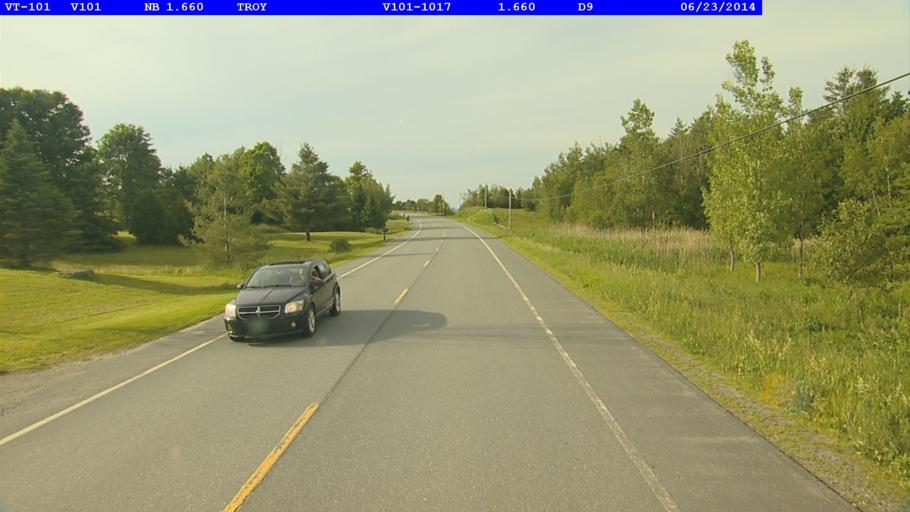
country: US
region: Vermont
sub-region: Orleans County
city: Newport
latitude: 44.9270
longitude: -72.4083
